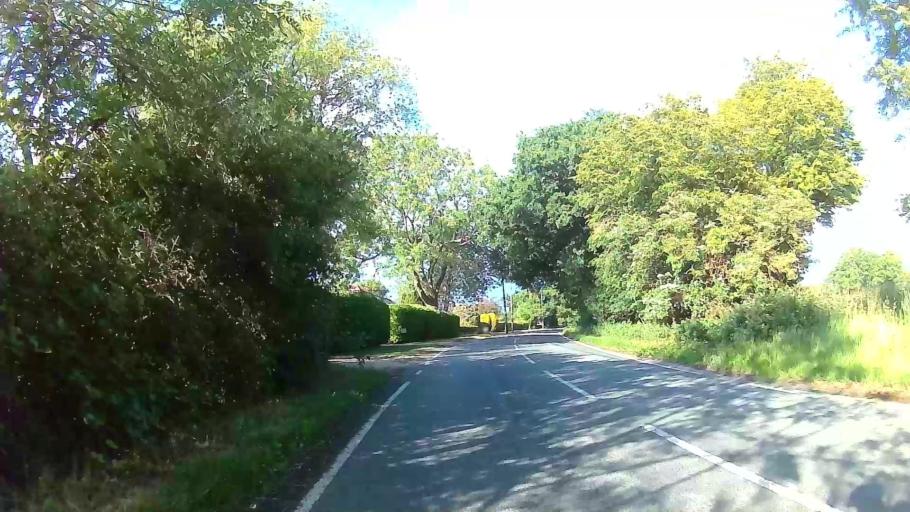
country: GB
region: England
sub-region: Essex
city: Kelvedon Hatch
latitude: 51.6791
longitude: 0.2978
